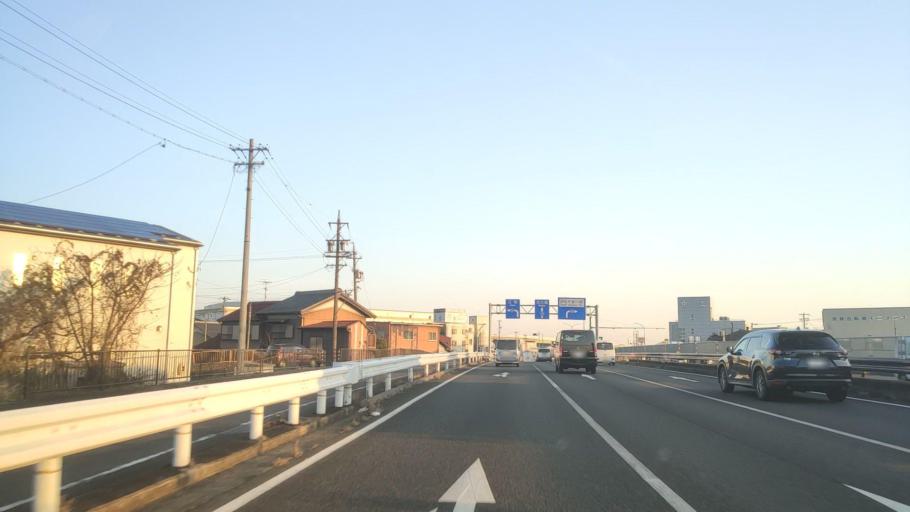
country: JP
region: Aichi
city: Kuroda
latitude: 35.3530
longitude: 136.7898
